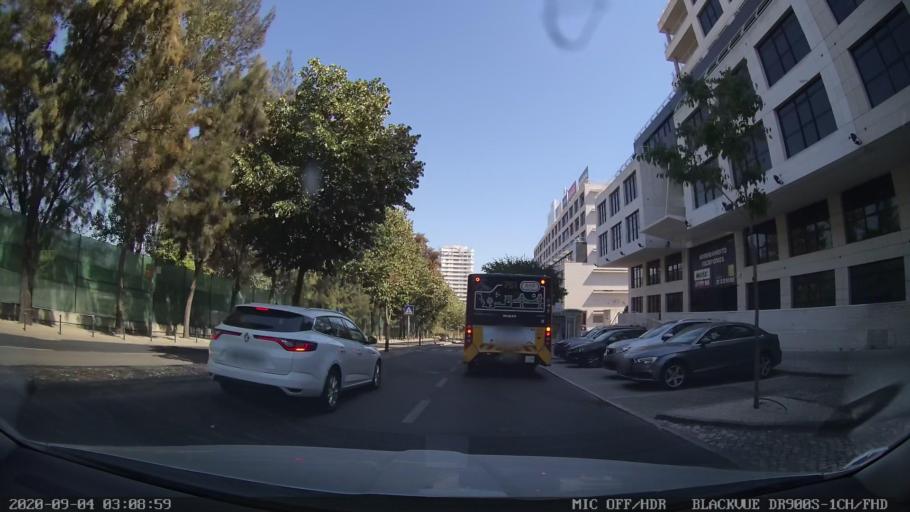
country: PT
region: Lisbon
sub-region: Oeiras
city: Linda-a-Velha
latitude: 38.7155
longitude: -9.2315
